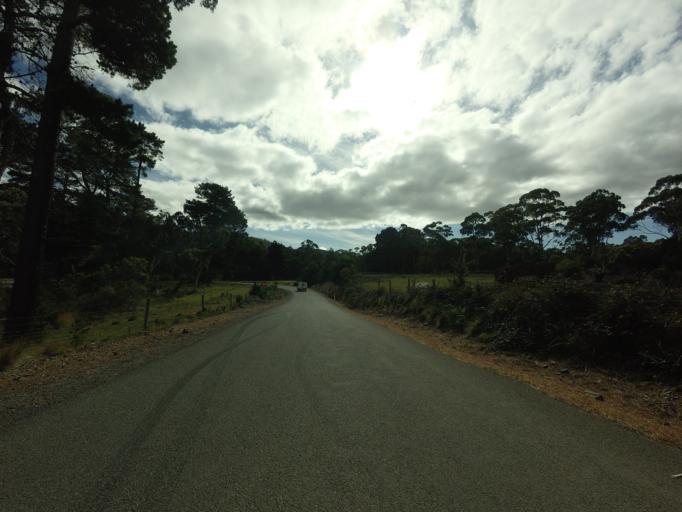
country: AU
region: Tasmania
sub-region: Clarence
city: Sandford
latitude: -43.0921
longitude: 147.7340
